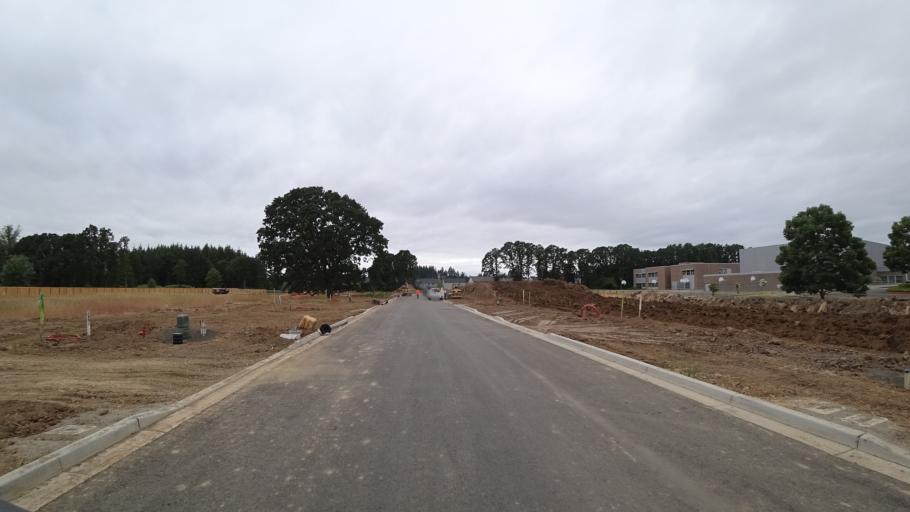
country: US
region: Oregon
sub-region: Washington County
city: Hillsboro
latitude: 45.4917
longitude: -122.9327
